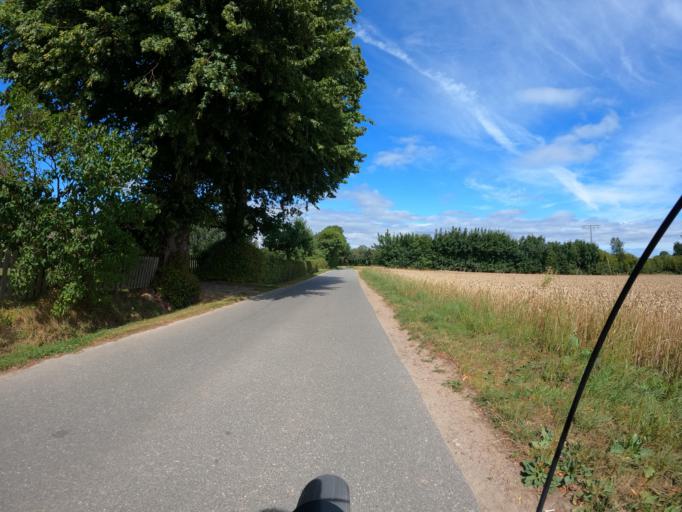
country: DE
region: Schleswig-Holstein
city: Steinbergkirche
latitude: 54.7814
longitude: 9.7609
